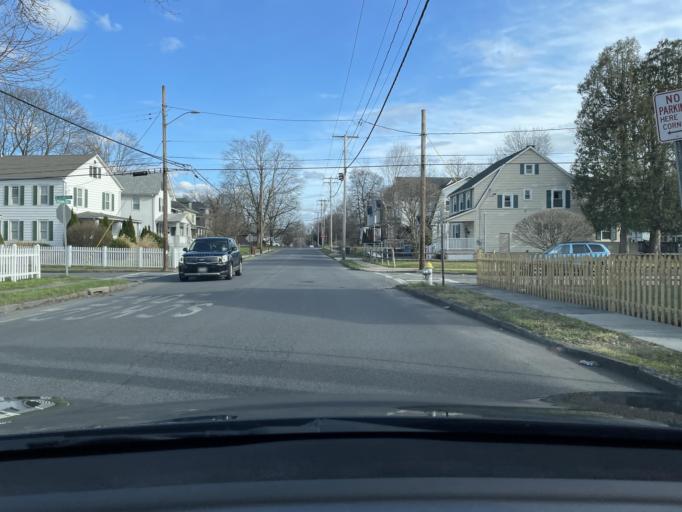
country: US
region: New York
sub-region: Ulster County
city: Kingston
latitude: 41.9247
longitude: -74.0153
